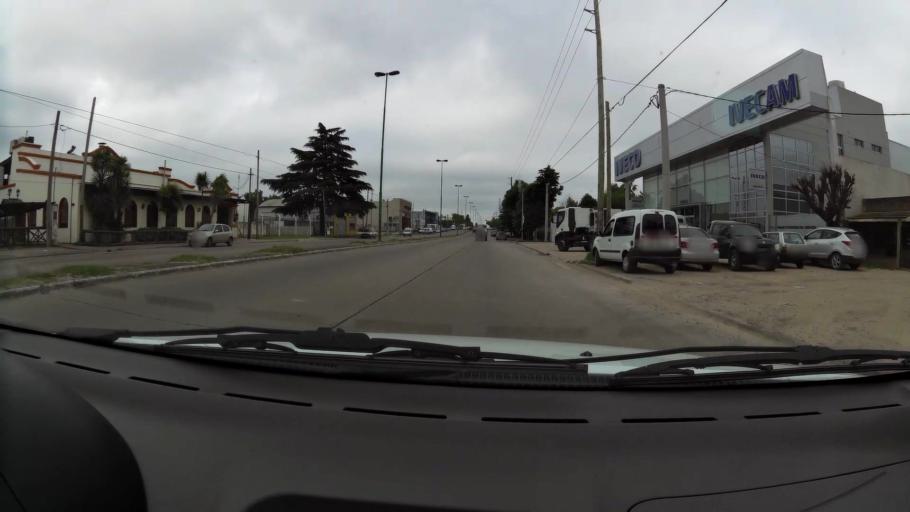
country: AR
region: Buenos Aires
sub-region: Partido de La Plata
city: La Plata
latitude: -34.9521
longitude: -58.0006
